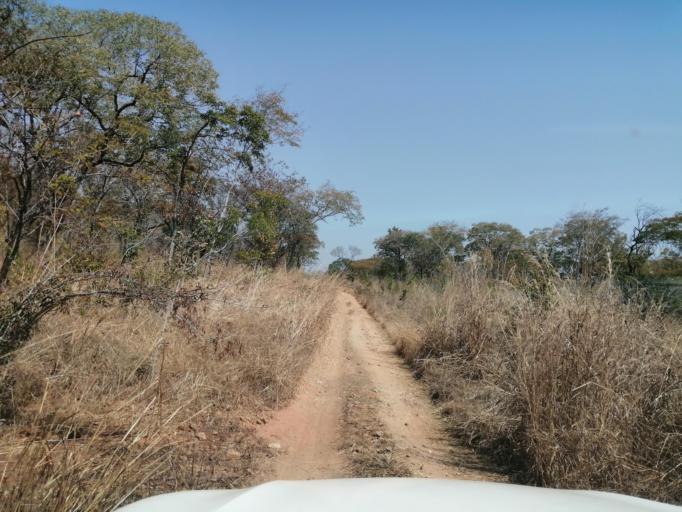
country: ZM
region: Eastern
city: Nyimba
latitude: -14.2574
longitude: 30.0810
